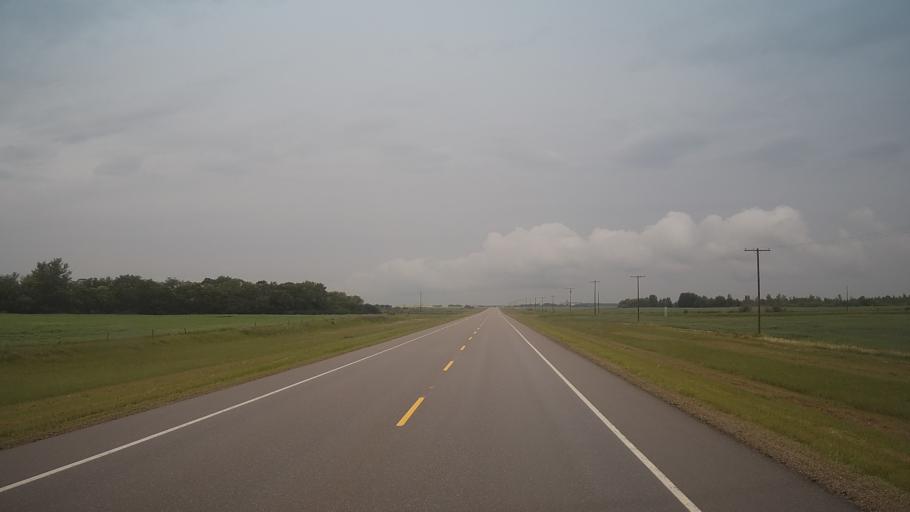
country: CA
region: Saskatchewan
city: Wilkie
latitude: 52.3163
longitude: -108.6979
